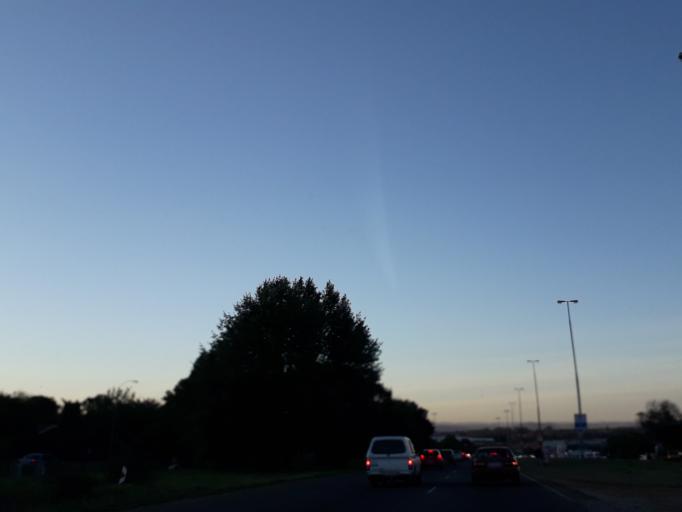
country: ZA
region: Gauteng
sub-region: City of Johannesburg Metropolitan Municipality
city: Roodepoort
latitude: -26.1359
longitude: 27.9159
